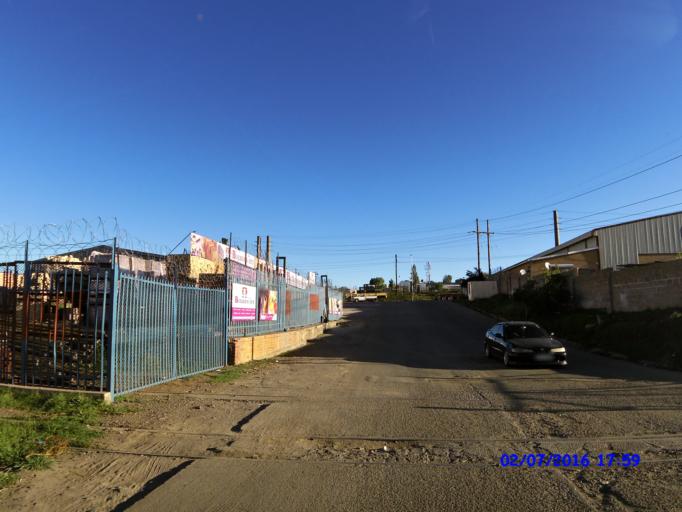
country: LS
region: Maseru
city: Maseru
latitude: -29.2959
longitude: 27.4790
